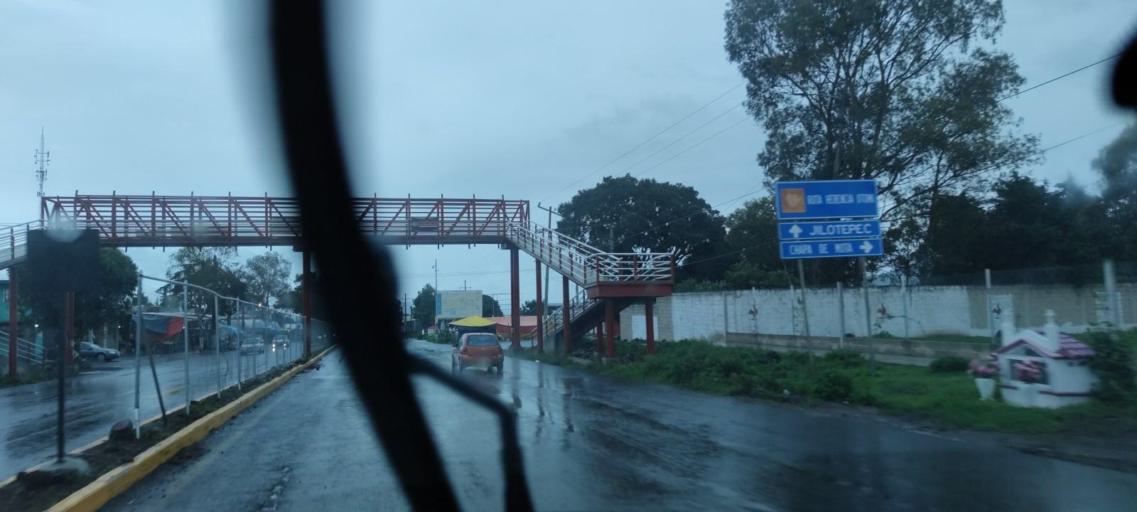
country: MX
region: Mexico
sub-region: Jilotepec
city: Doxhicho
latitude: 19.9260
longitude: -99.5825
